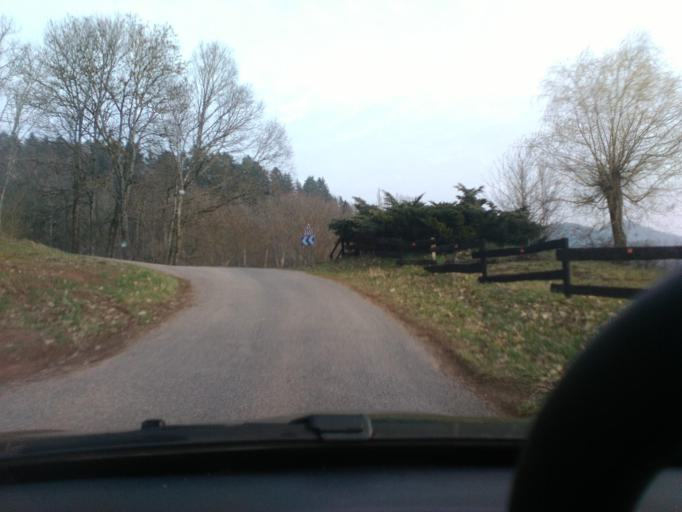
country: FR
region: Lorraine
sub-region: Departement des Vosges
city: Saint-Die-des-Vosges
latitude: 48.3012
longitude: 6.9465
